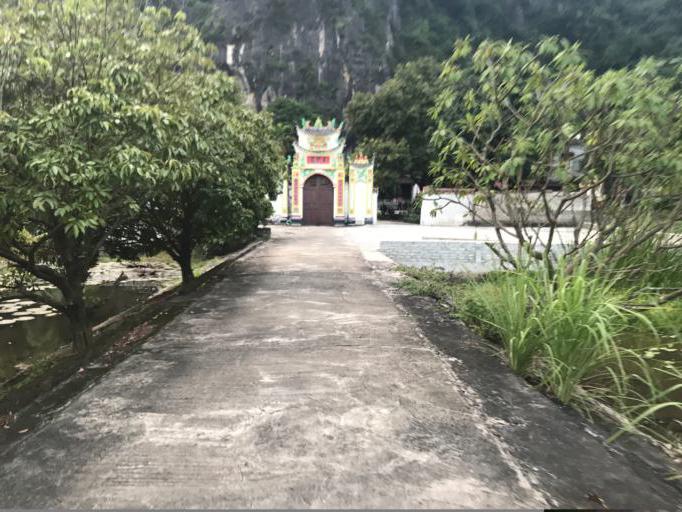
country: VN
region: Ninh Binh
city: Thi Tran Thien Ton
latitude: 20.2530
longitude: 105.9221
